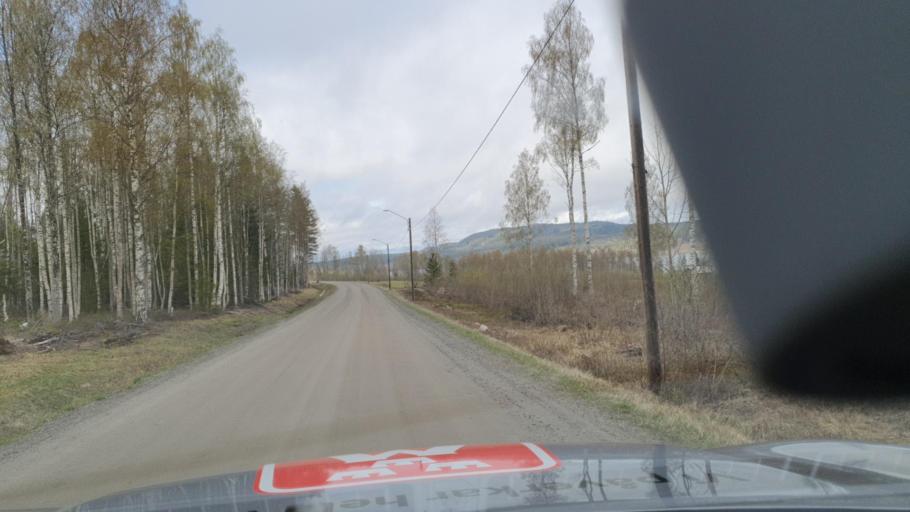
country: SE
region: Vaesterbotten
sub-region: Bjurholms Kommun
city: Bjurholm
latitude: 63.6593
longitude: 19.0302
